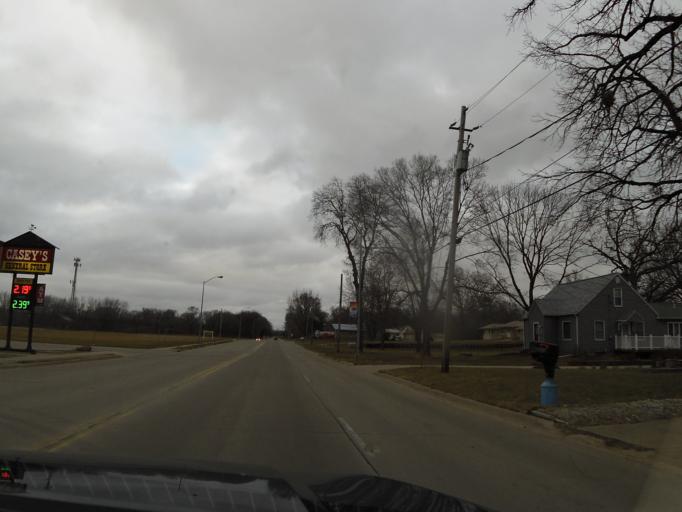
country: US
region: Iowa
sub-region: Black Hawk County
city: Evansdale
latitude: 42.4633
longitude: -92.2976
